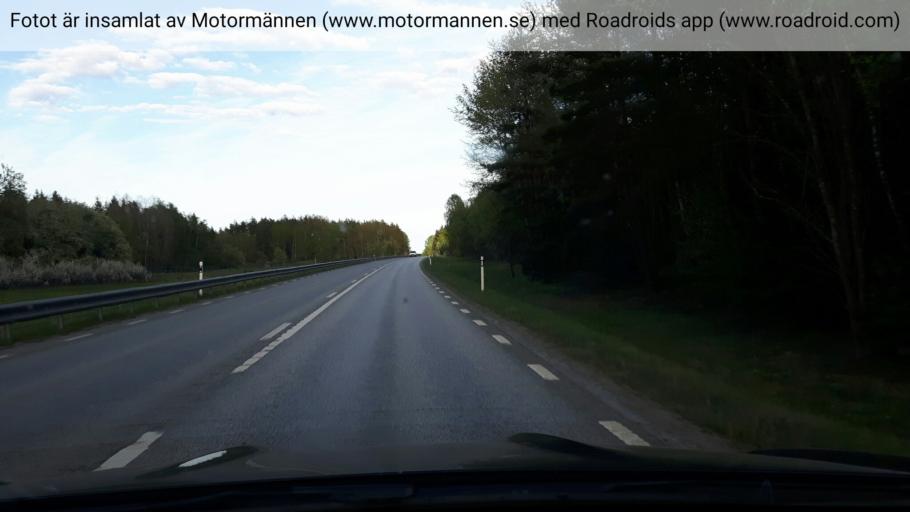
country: SE
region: Stockholm
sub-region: Osterakers Kommun
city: Akersberga
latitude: 59.4253
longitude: 18.2739
